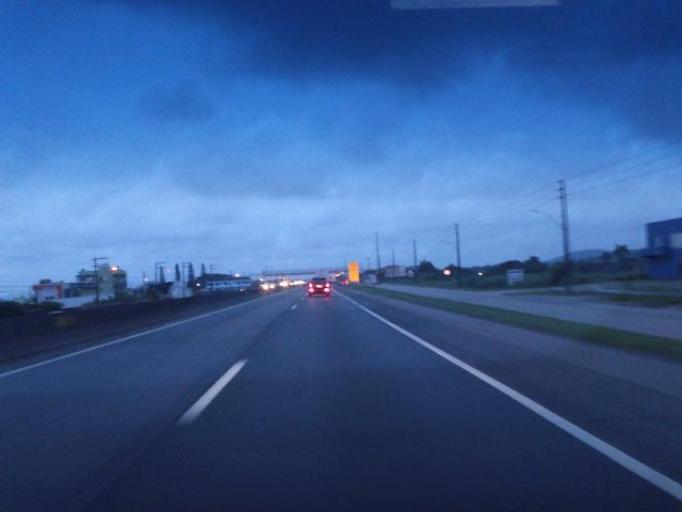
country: BR
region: Santa Catarina
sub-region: Barra Velha
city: Barra Velha
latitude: -26.6591
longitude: -48.6883
